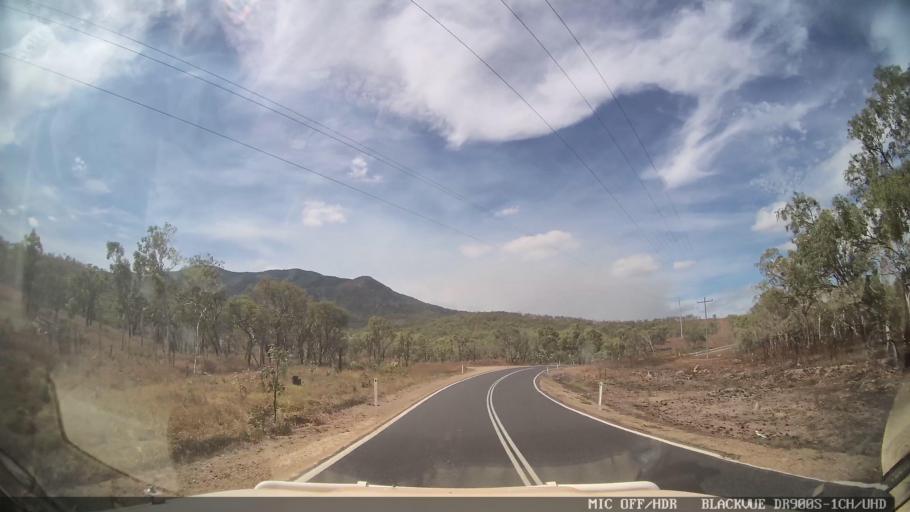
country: AU
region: Queensland
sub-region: Cairns
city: Port Douglas
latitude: -16.6690
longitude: 145.2639
